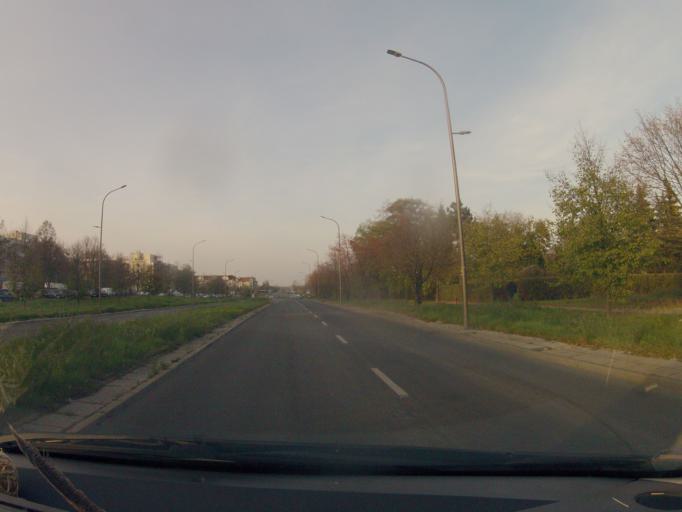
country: PL
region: Opole Voivodeship
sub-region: Powiat opolski
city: Opole
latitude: 50.6726
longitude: 17.9753
